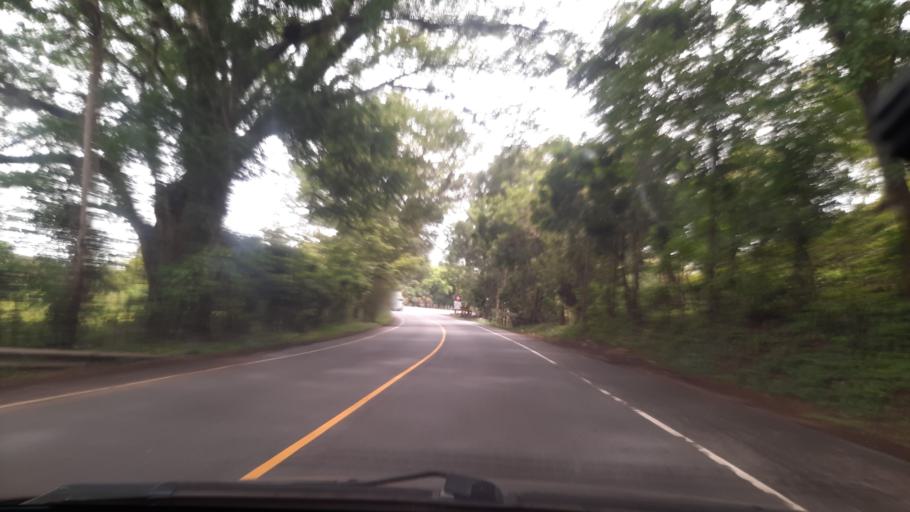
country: GT
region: Izabal
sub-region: Municipio de Los Amates
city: Los Amates
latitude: 15.2404
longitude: -89.1786
